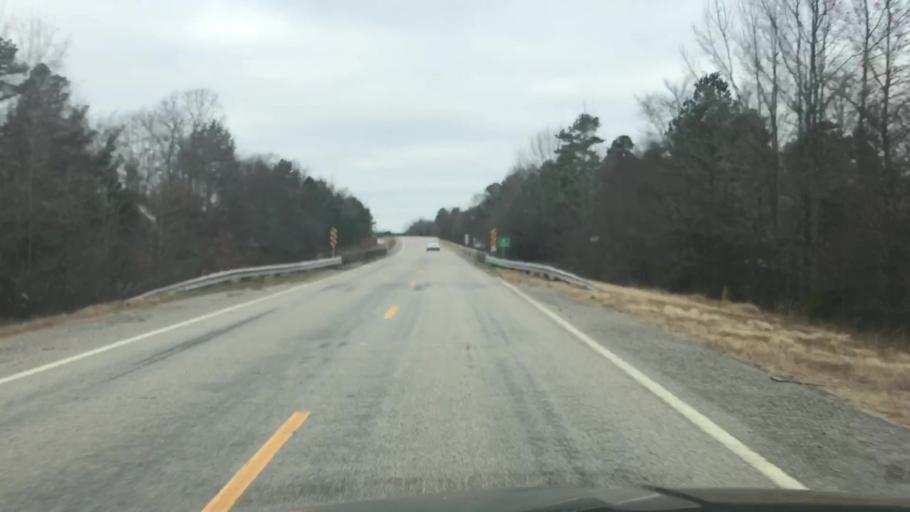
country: US
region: Arkansas
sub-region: Scott County
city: Waldron
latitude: 34.7012
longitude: -93.9165
